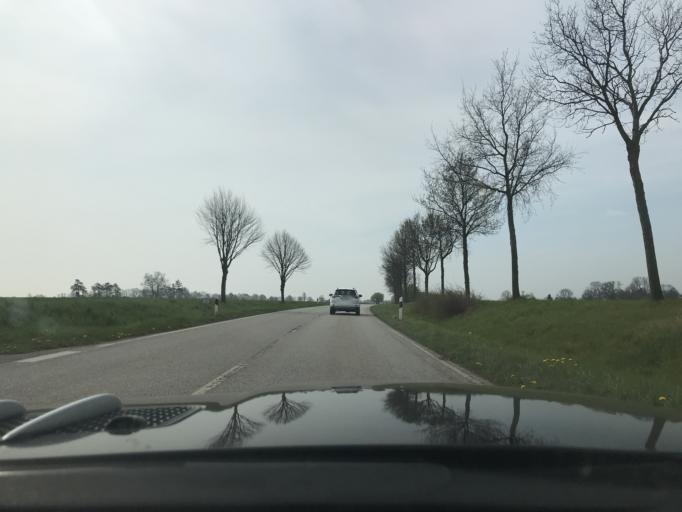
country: DE
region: Schleswig-Holstein
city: Grube
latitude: 54.2710
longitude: 11.0338
